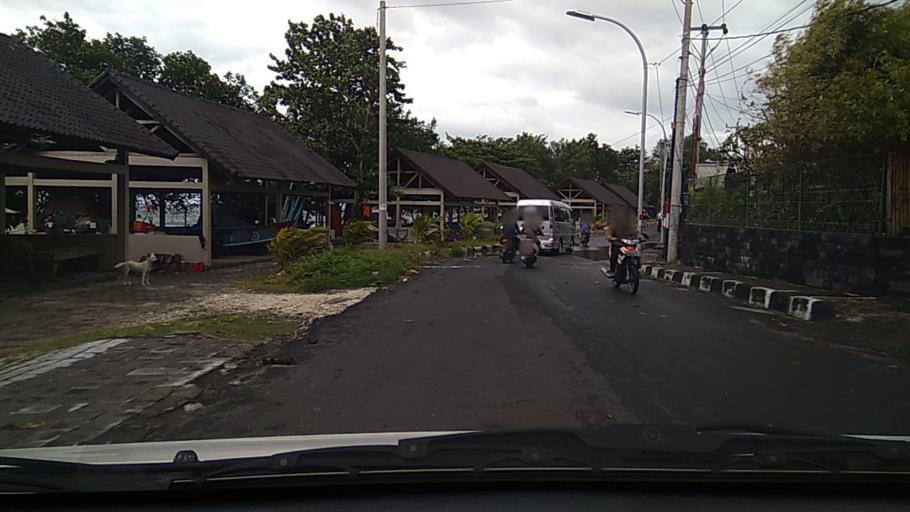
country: ID
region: Bali
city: Kelanabian
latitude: -8.7669
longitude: 115.1697
